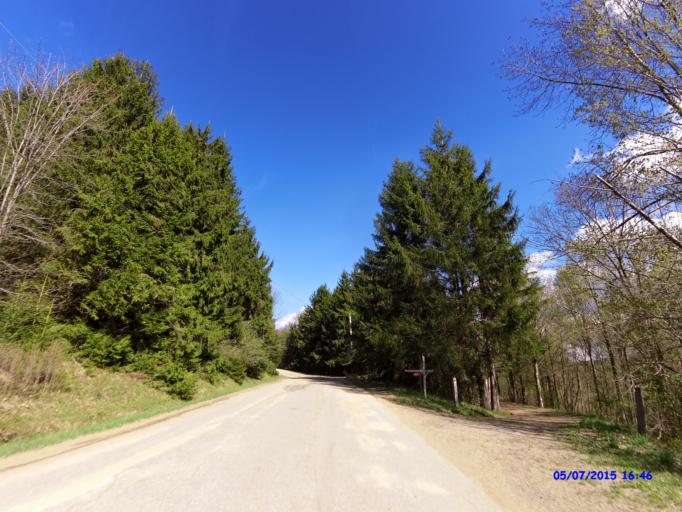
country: US
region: New York
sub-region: Cattaraugus County
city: Little Valley
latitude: 42.2848
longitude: -78.7036
